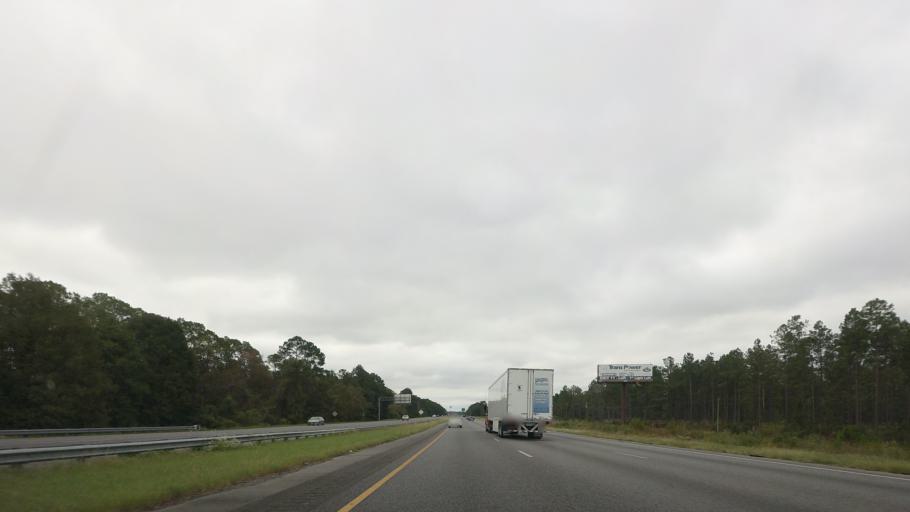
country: US
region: Georgia
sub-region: Lowndes County
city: Valdosta
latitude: 30.7692
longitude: -83.2896
